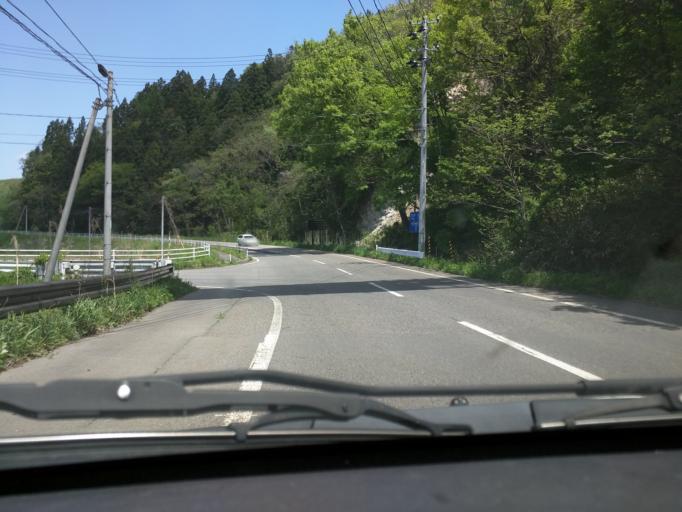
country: JP
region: Fukushima
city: Kitakata
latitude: 37.6406
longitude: 139.7789
